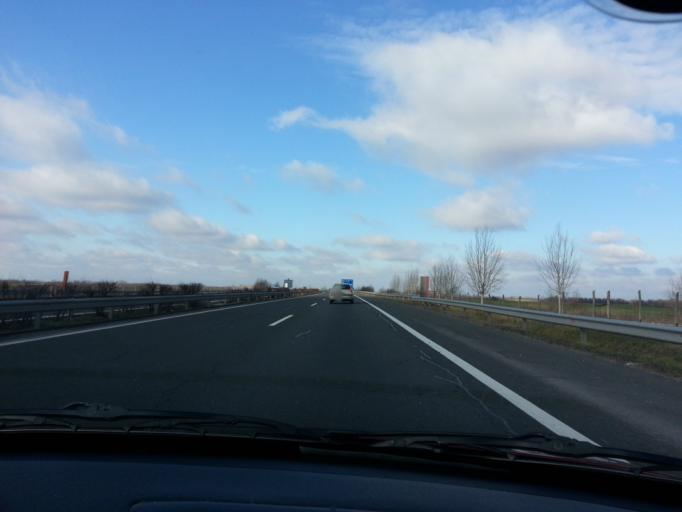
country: HU
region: Csongrad
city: Szatymaz
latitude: 46.2956
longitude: 20.0662
